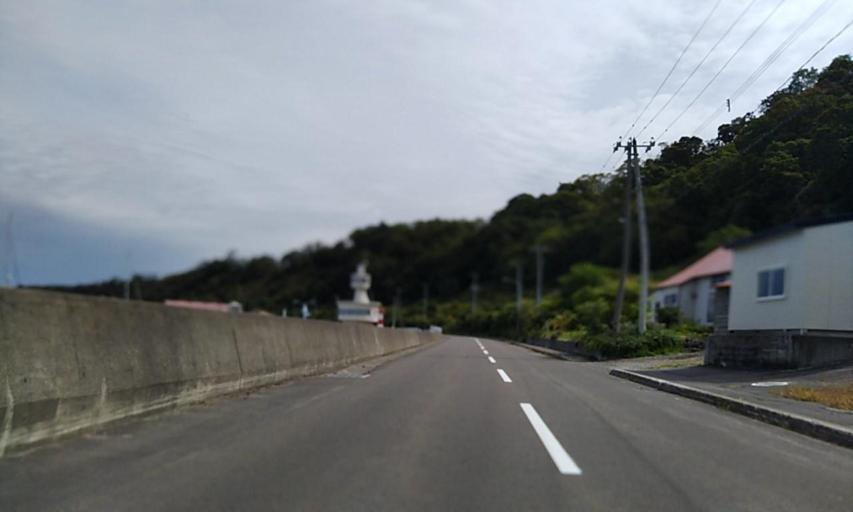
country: JP
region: Hokkaido
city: Rumoi
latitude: 43.8515
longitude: 141.5323
